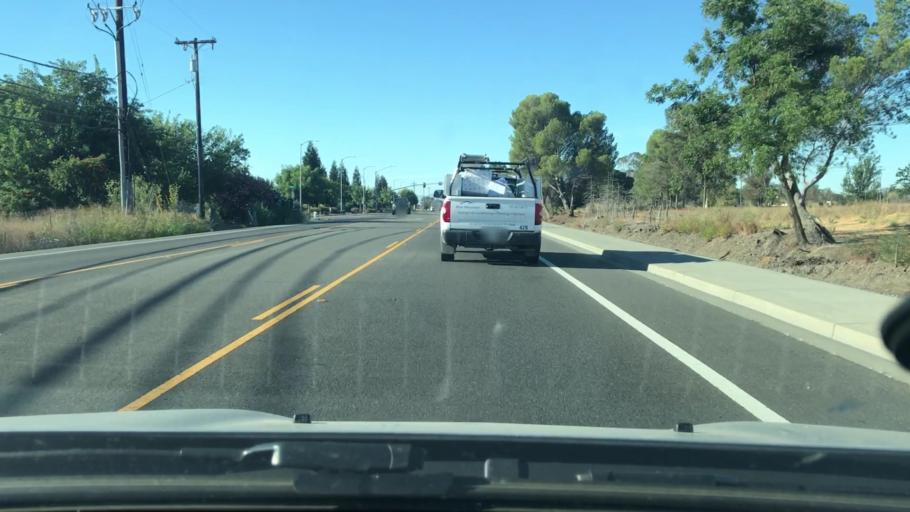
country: US
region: California
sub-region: Solano County
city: Hartley
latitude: 38.3764
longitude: -121.9339
